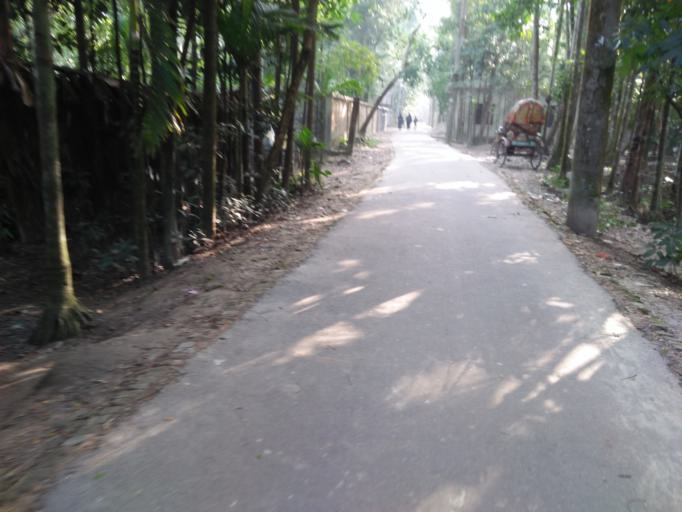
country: BD
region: Barisal
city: Bhola
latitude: 22.6766
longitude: 90.6375
